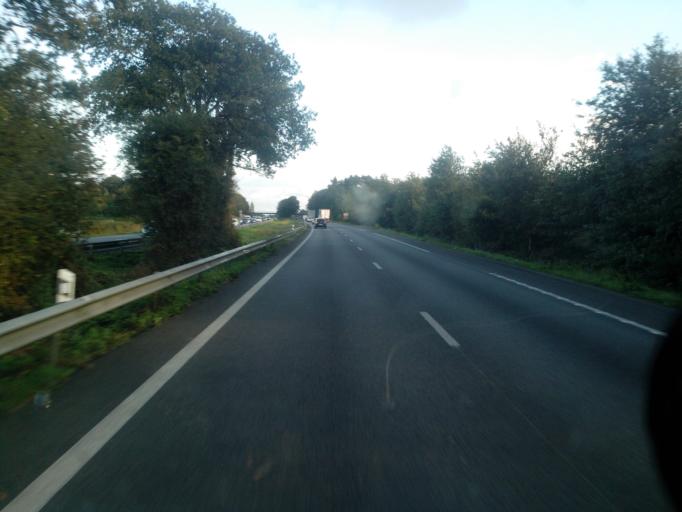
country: FR
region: Pays de la Loire
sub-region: Departement de la Loire-Atlantique
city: Vigneux-de-Bretagne
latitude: 47.3038
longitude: -1.7588
